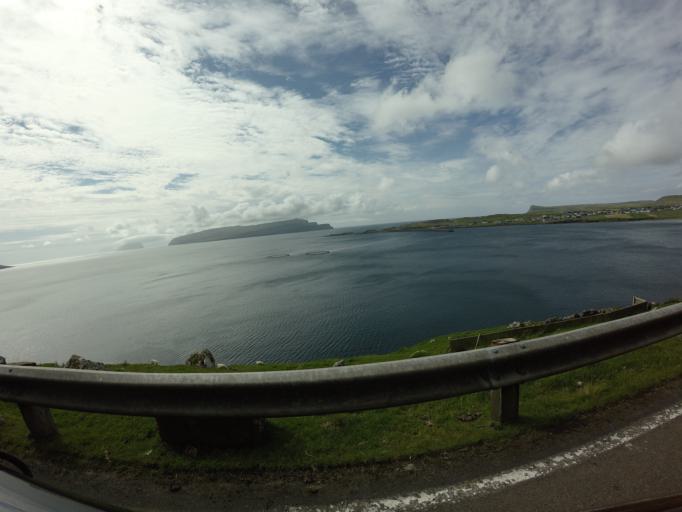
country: FO
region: Sandoy
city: Sandur
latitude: 61.8353
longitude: -6.7912
